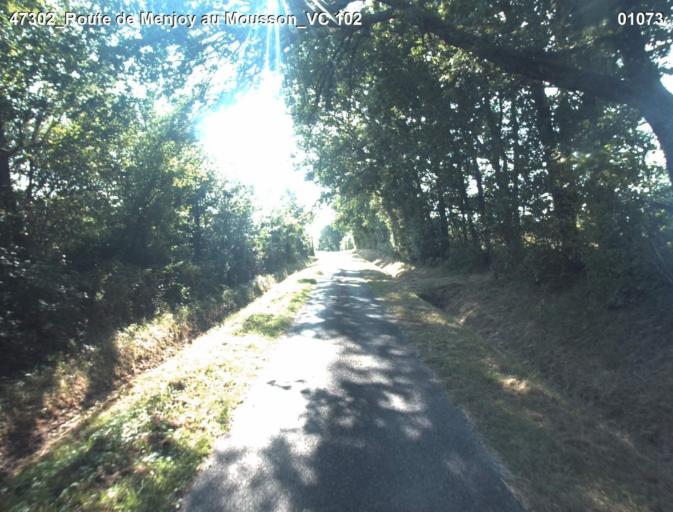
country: FR
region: Aquitaine
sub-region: Departement du Lot-et-Garonne
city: Mezin
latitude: 44.0529
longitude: 0.1765
